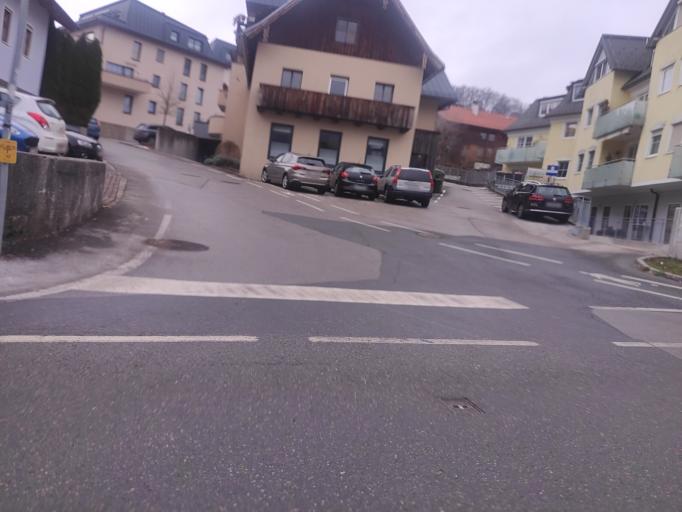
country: AT
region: Salzburg
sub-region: Politischer Bezirk Salzburg-Umgebung
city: Mattsee
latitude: 47.9689
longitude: 13.1039
